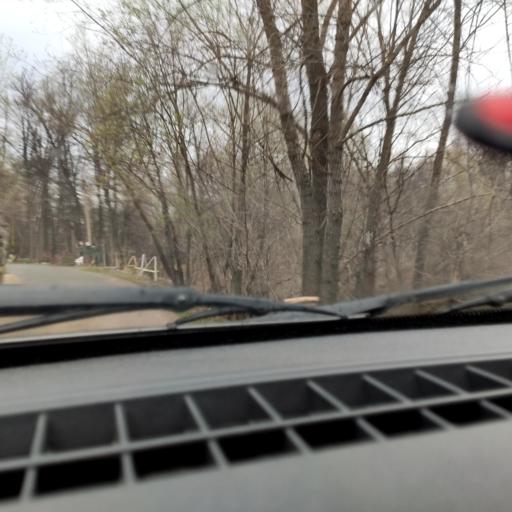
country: RU
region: Bashkortostan
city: Ufa
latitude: 54.6766
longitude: 56.0098
